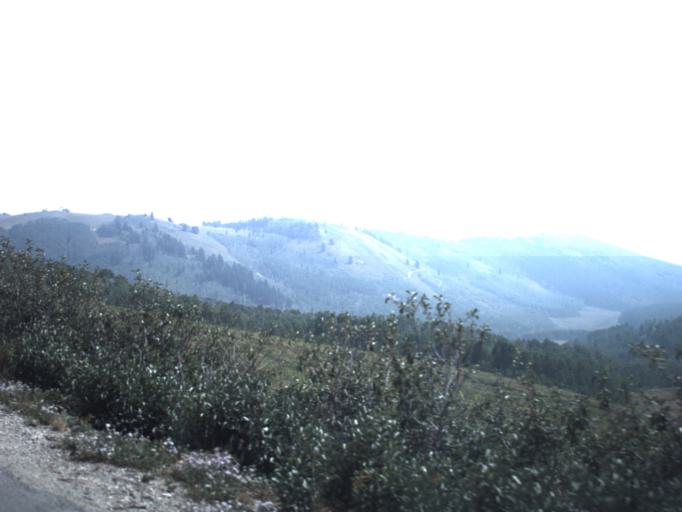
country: US
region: Utah
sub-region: Summit County
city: Park City
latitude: 40.6057
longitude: -111.5114
